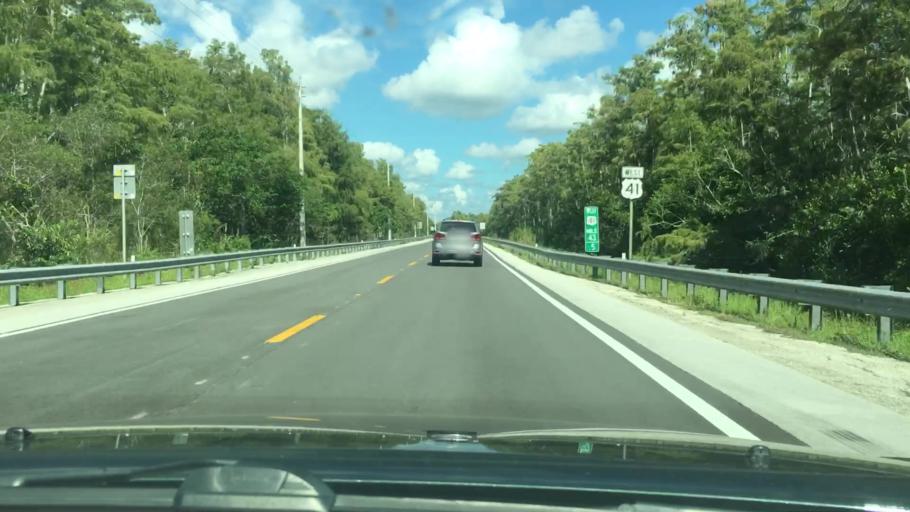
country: US
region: Florida
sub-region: Miami-Dade County
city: Kendall West
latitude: 25.8024
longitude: -80.8699
